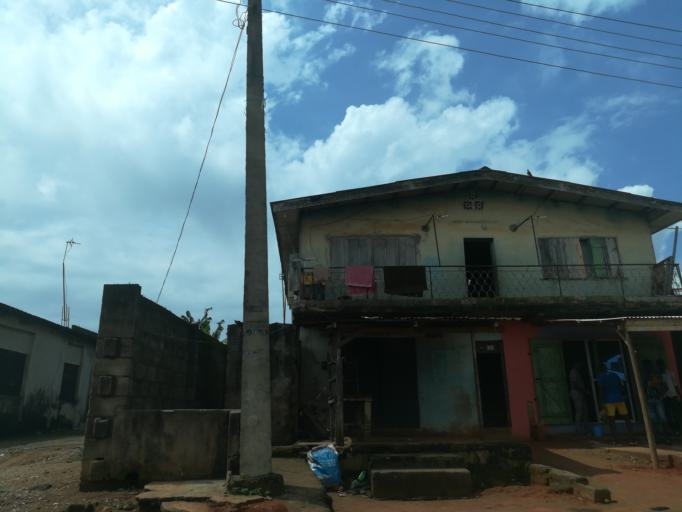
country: NG
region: Lagos
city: Ejirin
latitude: 6.6442
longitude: 3.7143
